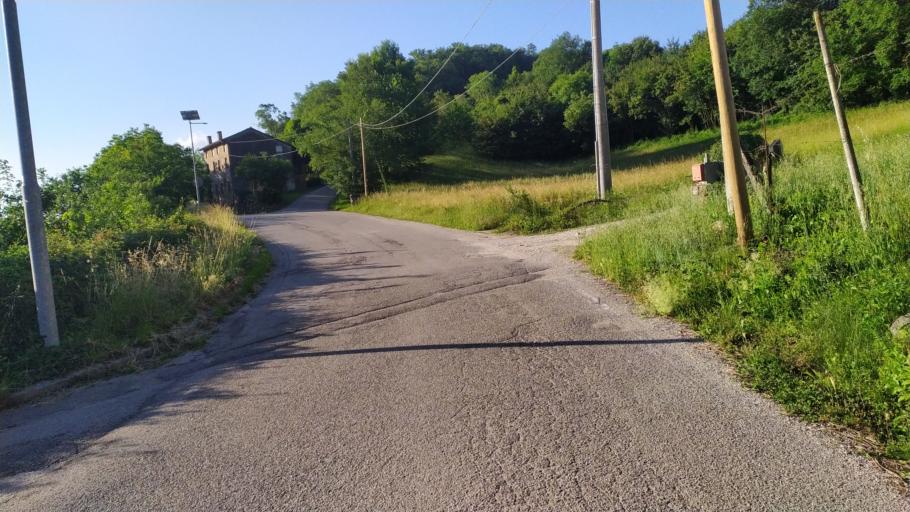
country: IT
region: Veneto
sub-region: Provincia di Vicenza
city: Malo
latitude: 45.6464
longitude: 11.4180
